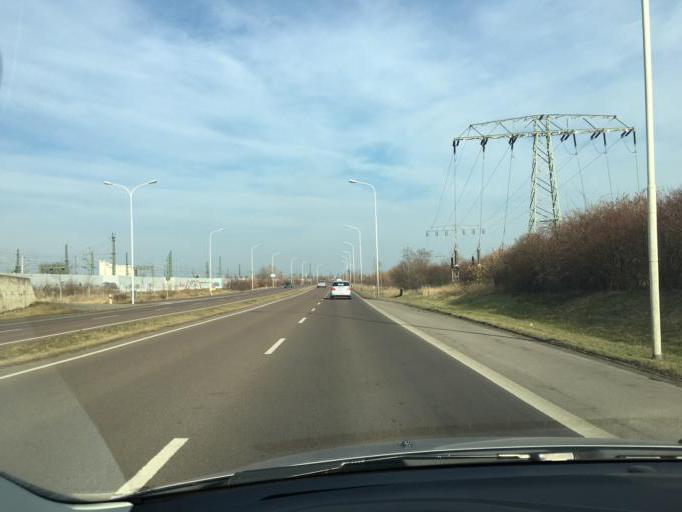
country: DE
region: Saxony-Anhalt
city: Halle (Saale)
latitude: 51.4583
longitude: 11.9957
